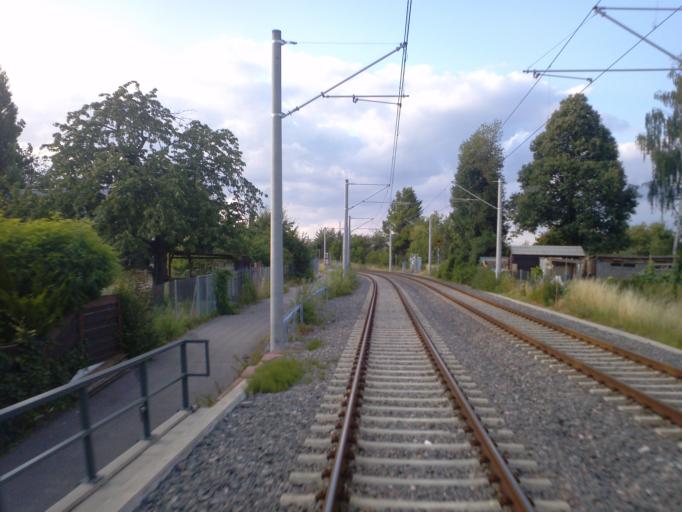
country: DE
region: Baden-Wuerttemberg
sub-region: Karlsruhe Region
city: Ettlingen
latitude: 48.9177
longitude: 8.5032
